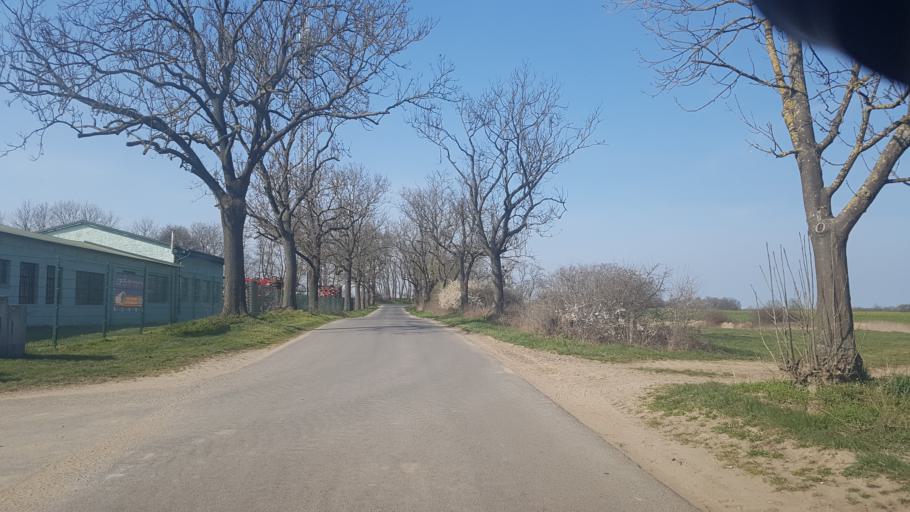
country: DE
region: Brandenburg
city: Gerswalde
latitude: 53.1898
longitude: 13.7797
